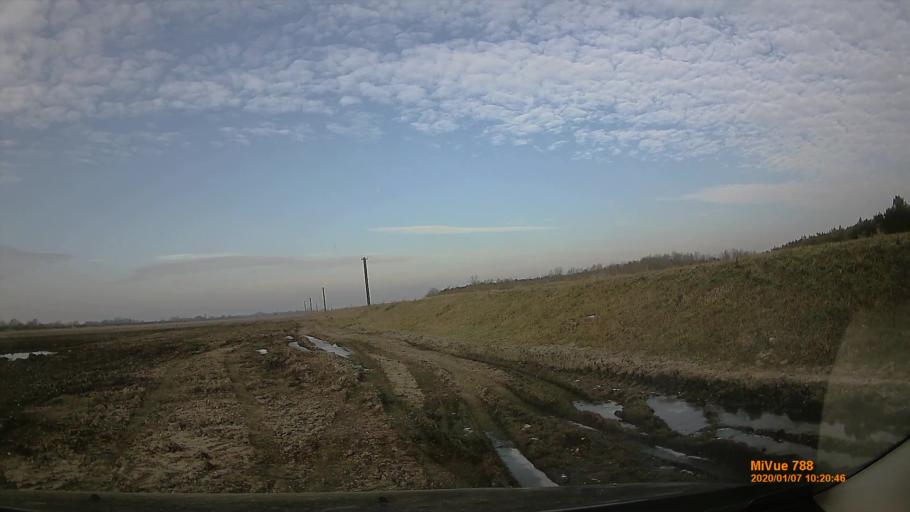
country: HU
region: Gyor-Moson-Sopron
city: Rajka
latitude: 47.9214
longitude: 17.1933
